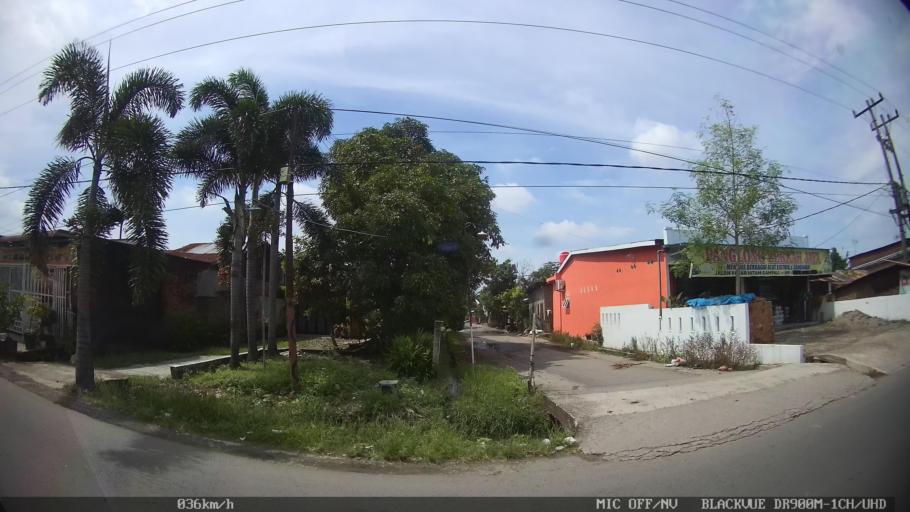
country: ID
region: North Sumatra
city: Medan
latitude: 3.6283
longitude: 98.7092
